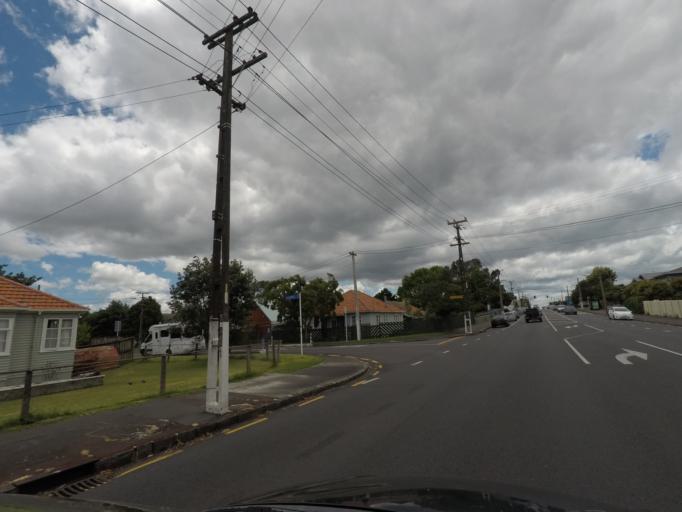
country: NZ
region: Auckland
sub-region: Auckland
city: Auckland
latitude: -36.8894
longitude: 174.7370
